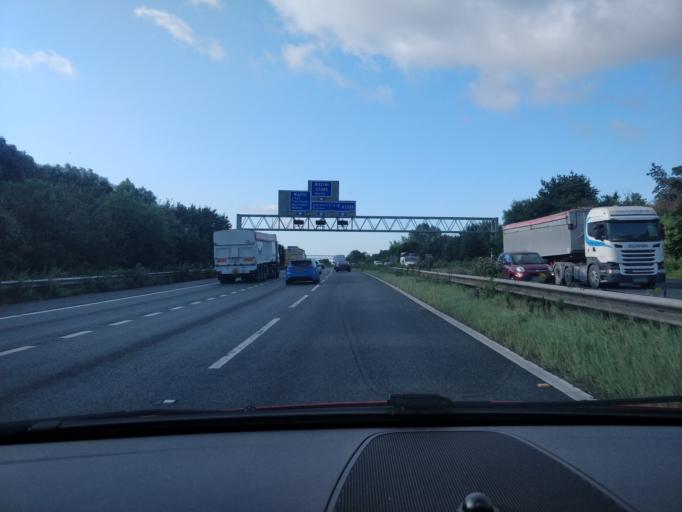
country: GB
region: England
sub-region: Knowsley
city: Prescot
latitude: 53.4085
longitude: -2.8140
